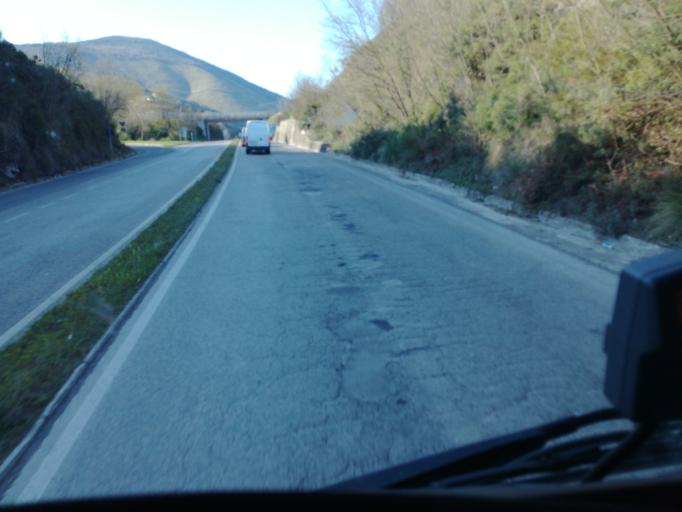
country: IT
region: Latium
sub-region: Provincia di Frosinone
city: Giuliano di Roma
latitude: 41.5480
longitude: 13.2692
